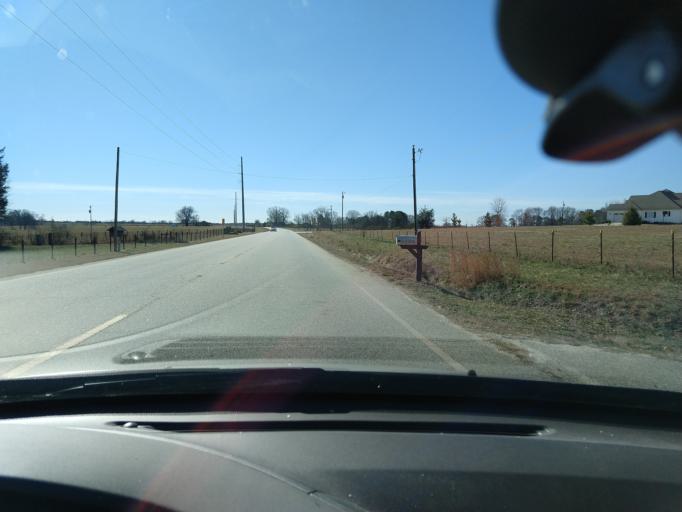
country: US
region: Georgia
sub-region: Walton County
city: Social Circle
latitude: 33.5059
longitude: -83.7354
